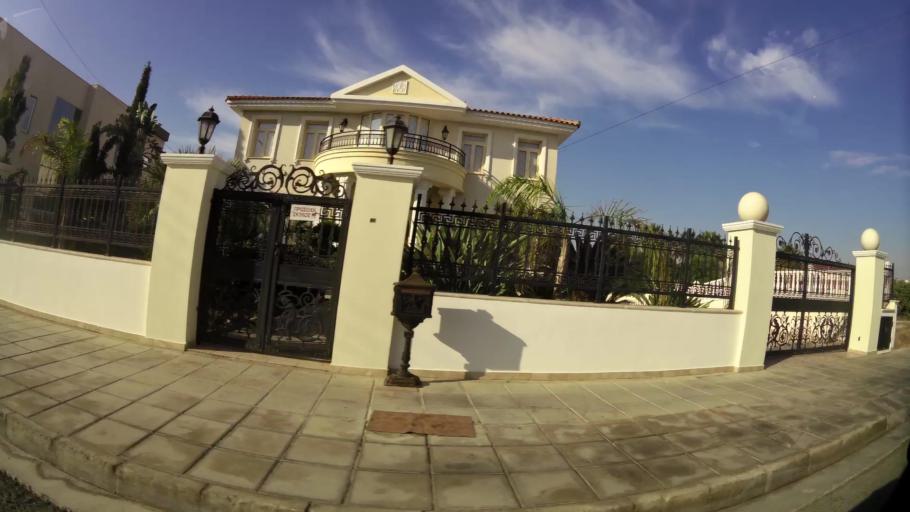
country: CY
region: Larnaka
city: Aradippou
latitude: 34.9375
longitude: 33.5973
